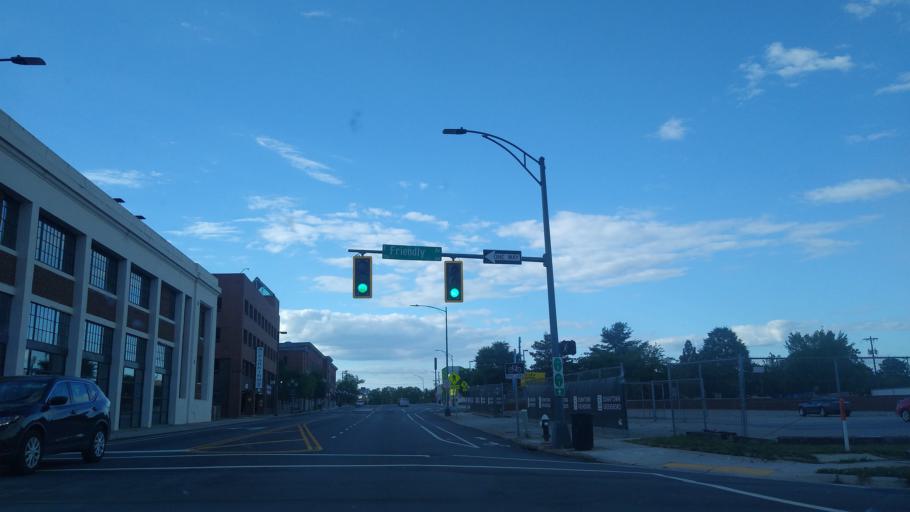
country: US
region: North Carolina
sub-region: Guilford County
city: Greensboro
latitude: 36.0733
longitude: -79.7867
